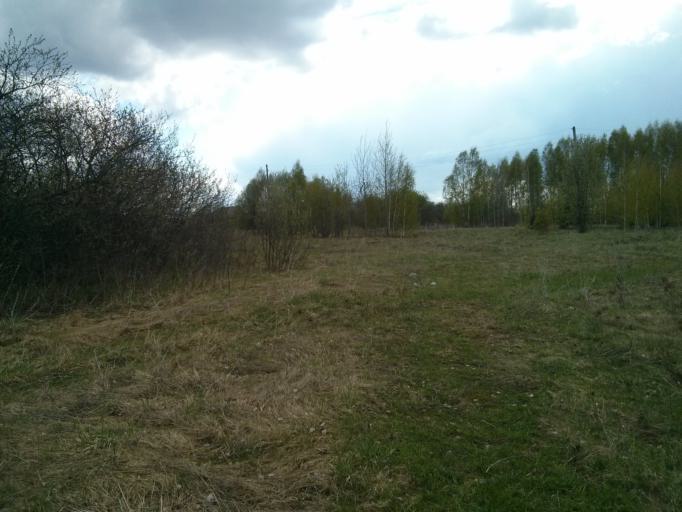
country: RU
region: Nizjnij Novgorod
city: Shimorskoye
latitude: 55.3075
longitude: 41.8445
